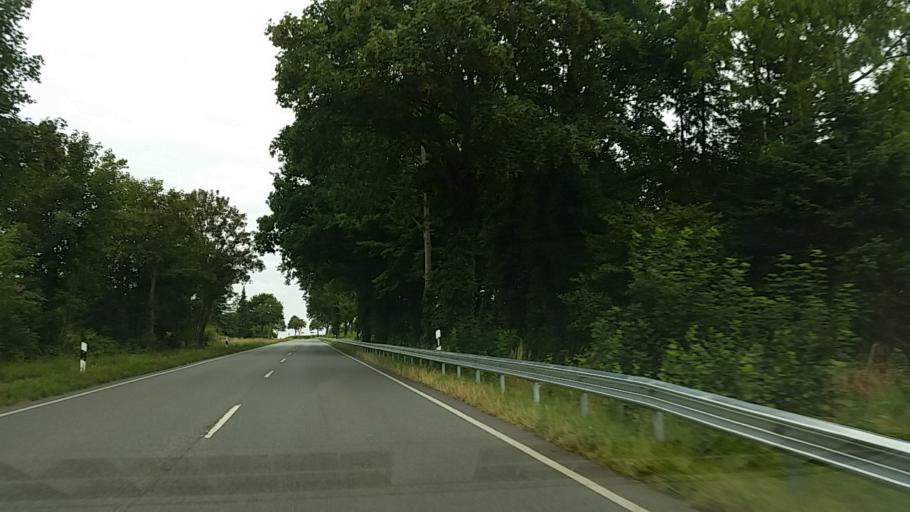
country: DE
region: Lower Saxony
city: Beverstedt
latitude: 53.4276
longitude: 8.8837
